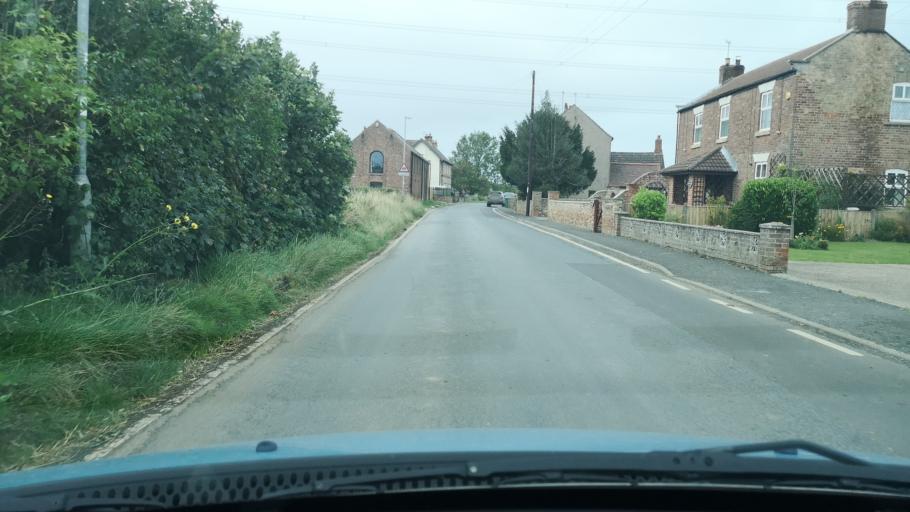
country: GB
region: England
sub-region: East Riding of Yorkshire
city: Laxton
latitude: 53.6983
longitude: -0.7440
